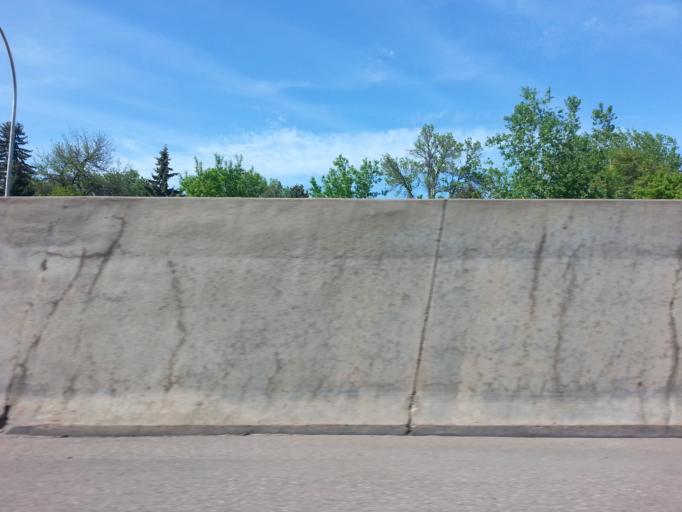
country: US
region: Minnesota
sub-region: Ramsey County
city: Little Canada
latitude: 45.0096
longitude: -93.0791
